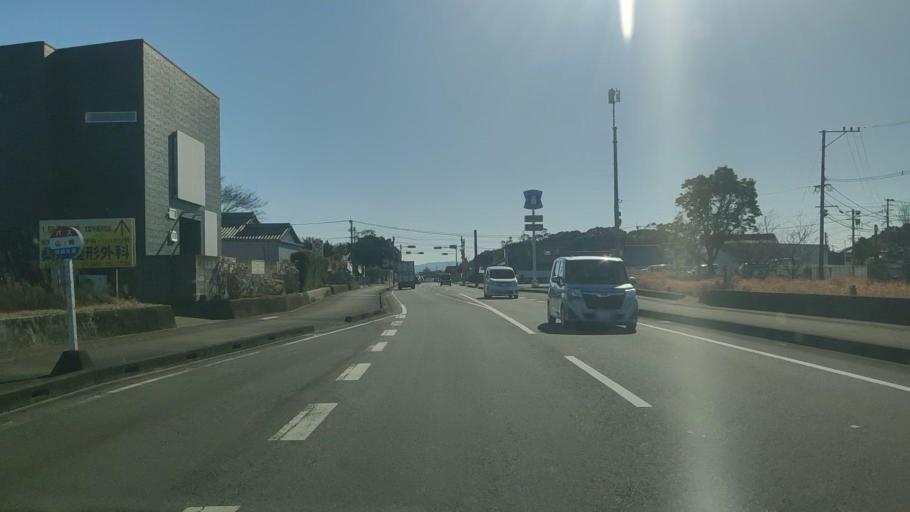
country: JP
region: Miyazaki
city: Miyazaki-shi
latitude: 31.9526
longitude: 131.4605
